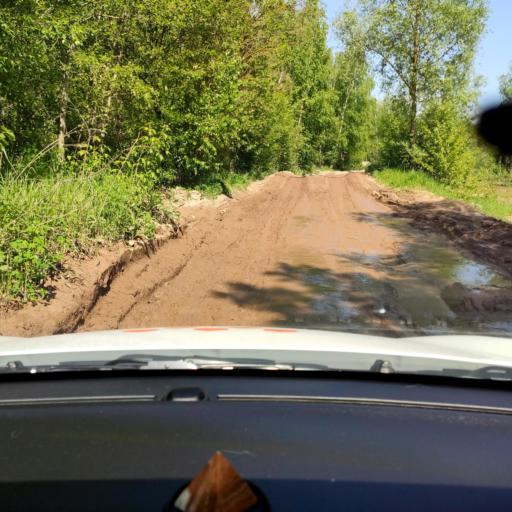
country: RU
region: Tatarstan
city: Stolbishchi
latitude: 55.7067
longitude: 49.1850
